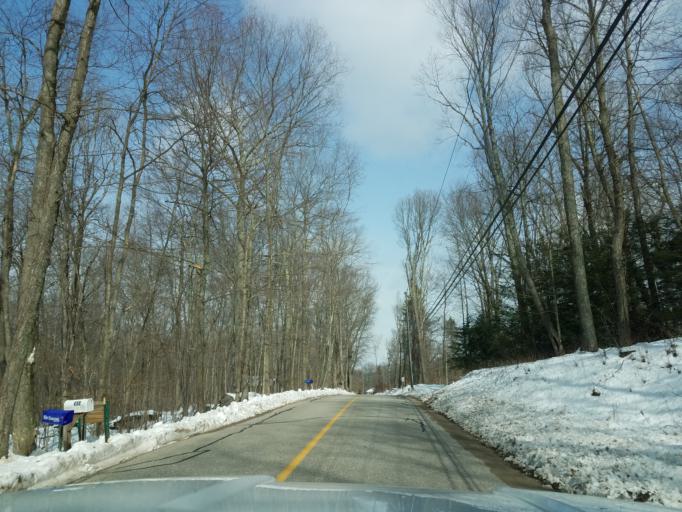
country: US
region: Connecticut
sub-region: Tolland County
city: Coventry Lake
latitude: 41.7231
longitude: -72.3554
